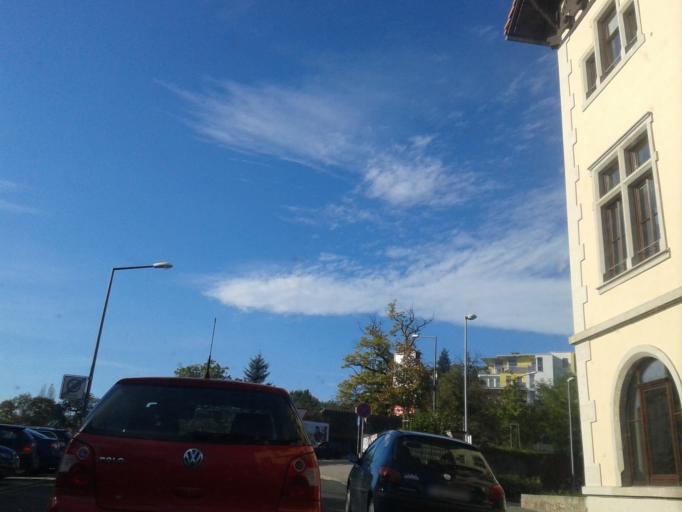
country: DE
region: Saxony
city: Albertstadt
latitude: 51.0965
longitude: 13.7197
